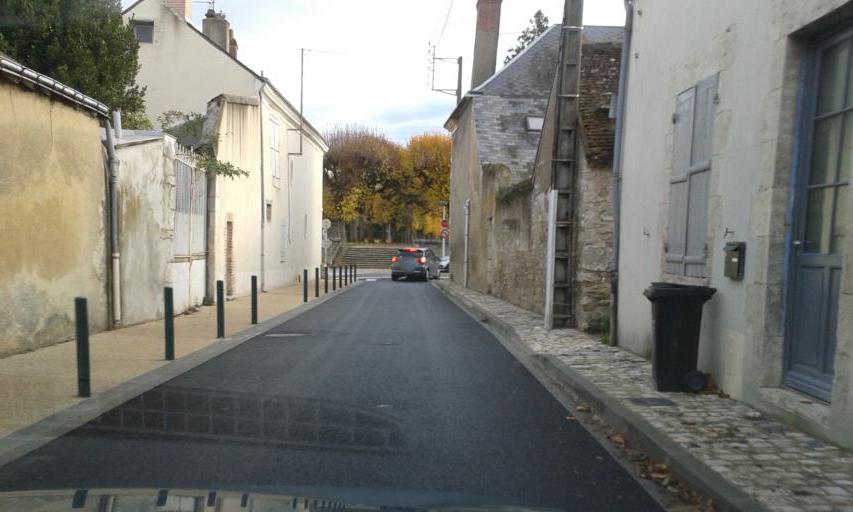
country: FR
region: Centre
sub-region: Departement du Loiret
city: Beaugency
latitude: 47.7781
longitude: 1.6271
